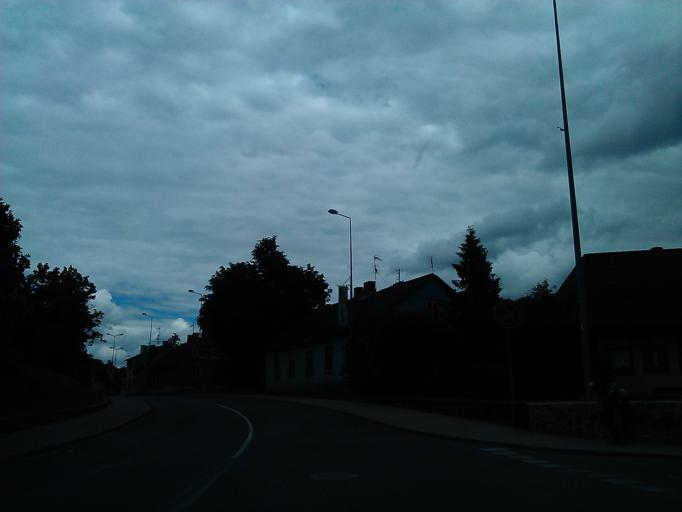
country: LV
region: Dobeles Rajons
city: Dobele
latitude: 56.6236
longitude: 23.2753
